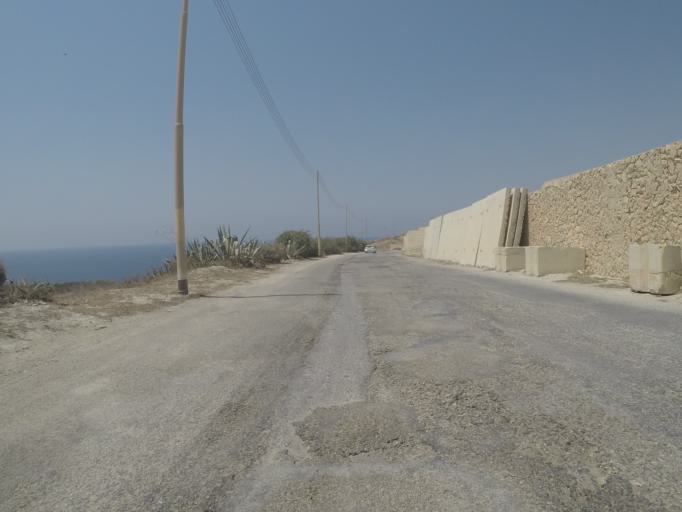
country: MT
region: Is-Siggiewi
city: Siggiewi
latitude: 35.8343
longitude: 14.4188
